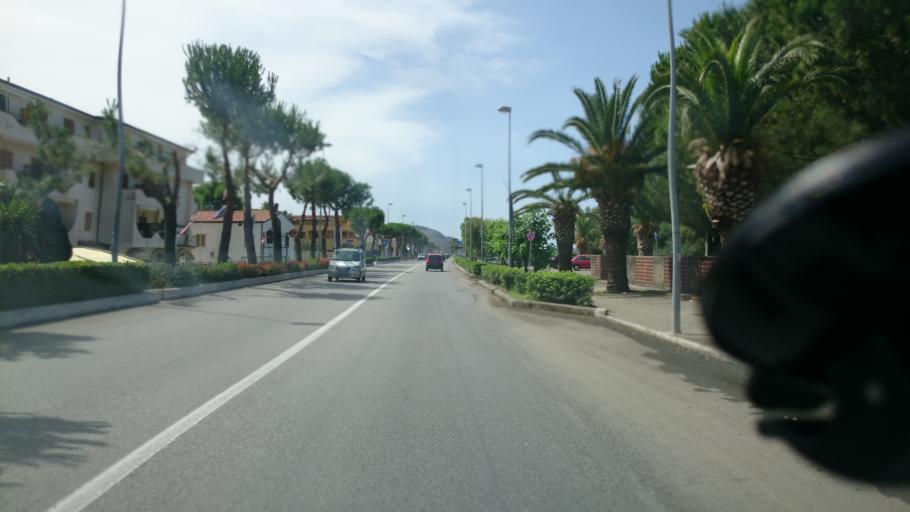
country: IT
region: Calabria
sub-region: Provincia di Cosenza
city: Marcellina
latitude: 39.7513
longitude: 15.8054
